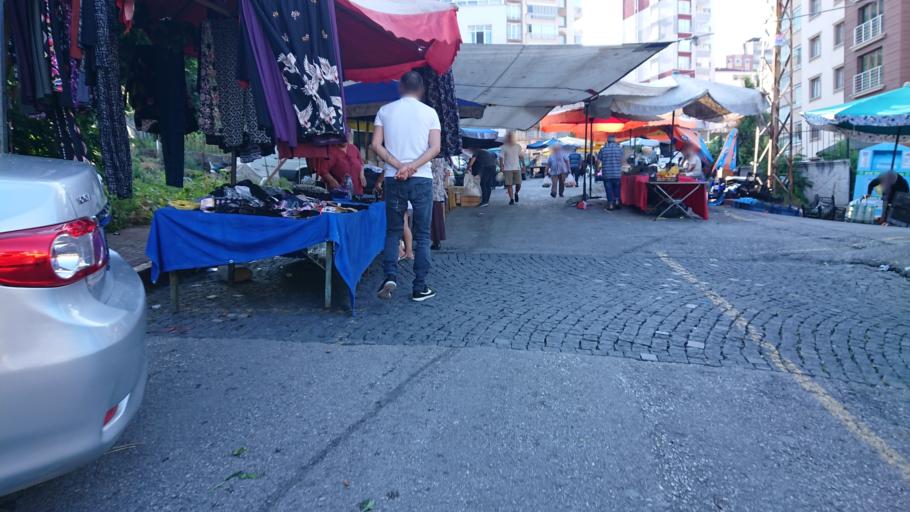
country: TR
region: Samsun
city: Samsun
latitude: 41.2995
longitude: 36.3217
